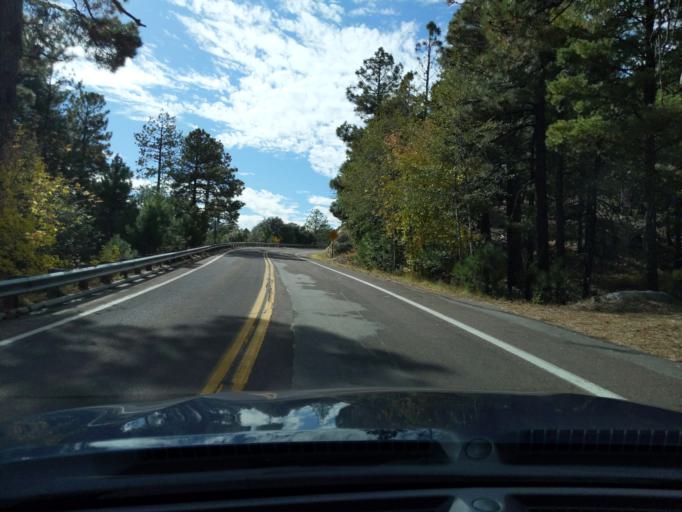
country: US
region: Arizona
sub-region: Pima County
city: Tanque Verde
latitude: 32.4109
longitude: -110.7156
